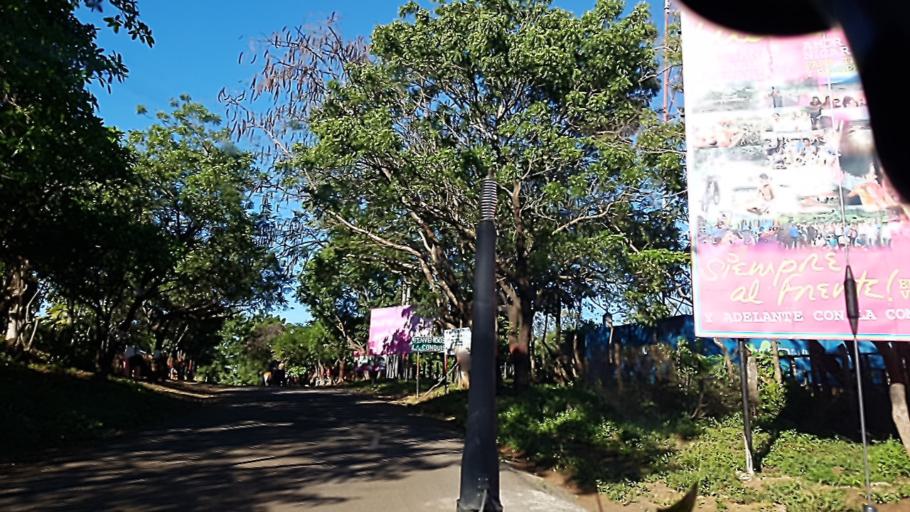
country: NI
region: Carazo
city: Santa Teresa
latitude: 11.7355
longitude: -86.1895
